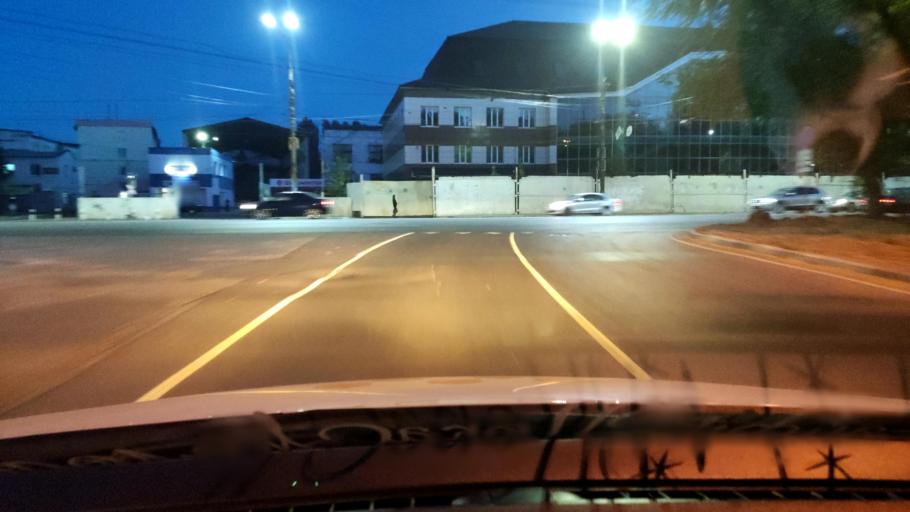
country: RU
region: Voronezj
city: Voronezh
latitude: 51.6759
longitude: 39.1689
